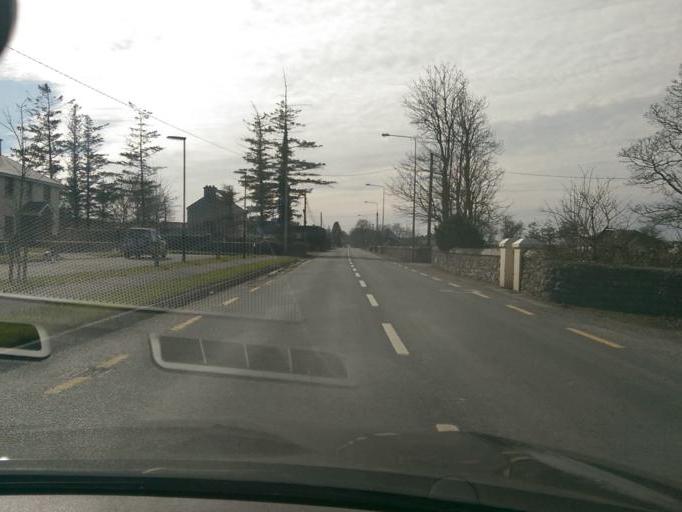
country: IE
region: Connaught
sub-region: County Galway
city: Tuam
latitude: 53.4350
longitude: -8.7527
